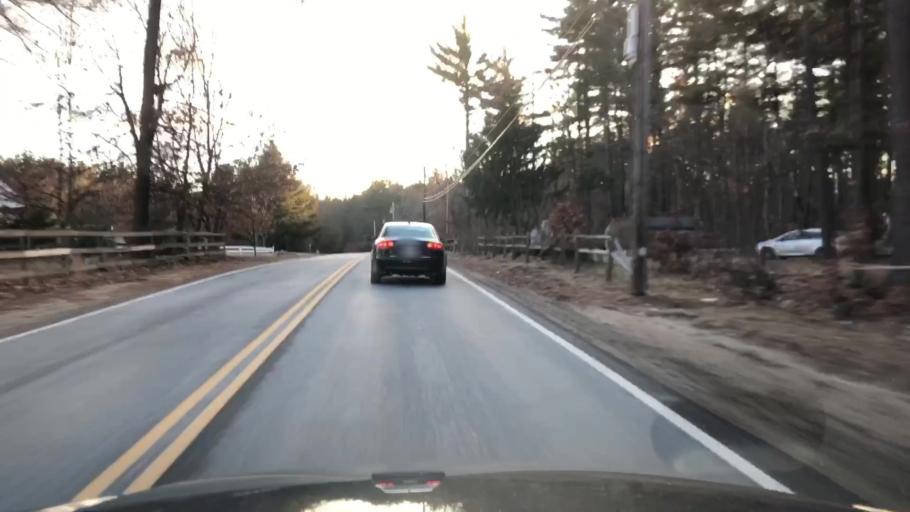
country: US
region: Massachusetts
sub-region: Middlesex County
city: Townsend
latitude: 42.6834
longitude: -71.6956
